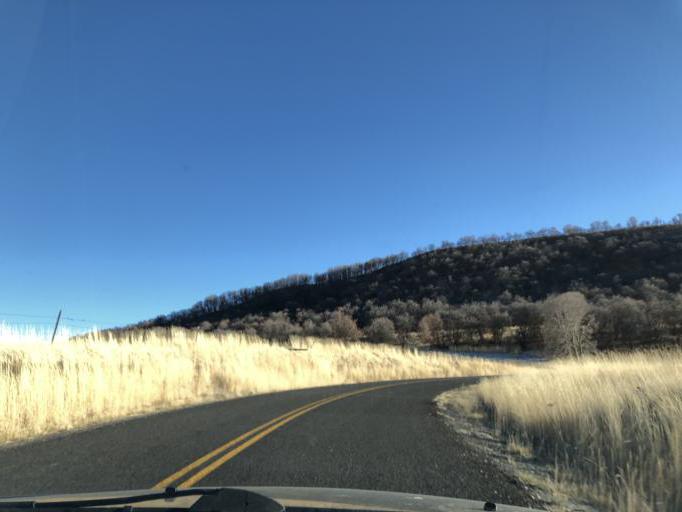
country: US
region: Utah
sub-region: Cache County
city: Wellsville
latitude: 41.5791
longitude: -111.9209
